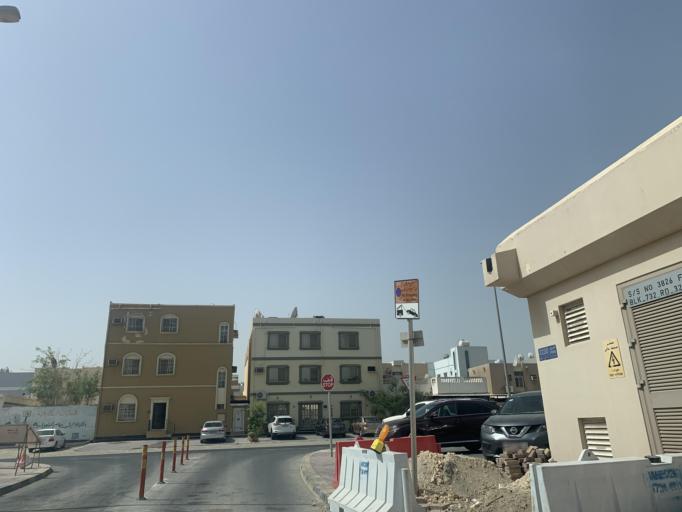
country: BH
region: Northern
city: Madinat `Isa
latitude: 26.1524
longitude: 50.5264
